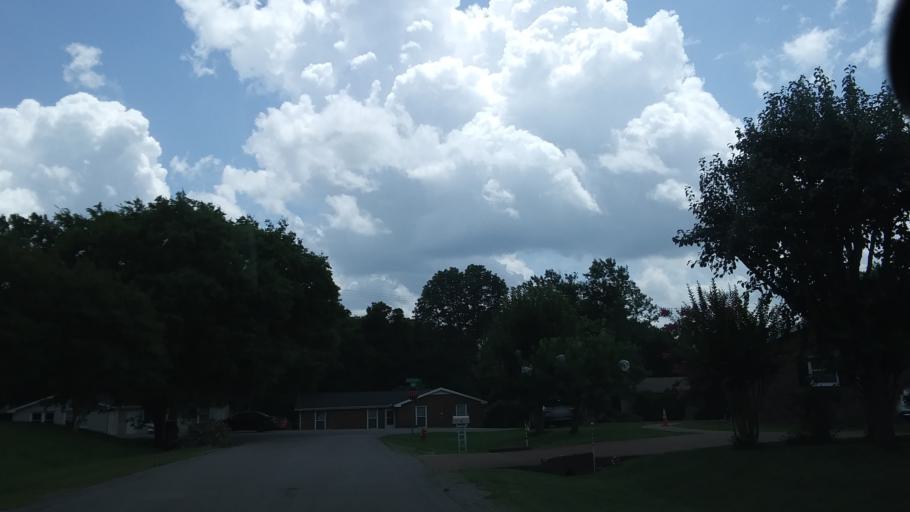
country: US
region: Tennessee
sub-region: Davidson County
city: Belle Meade
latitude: 36.1436
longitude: -86.8851
